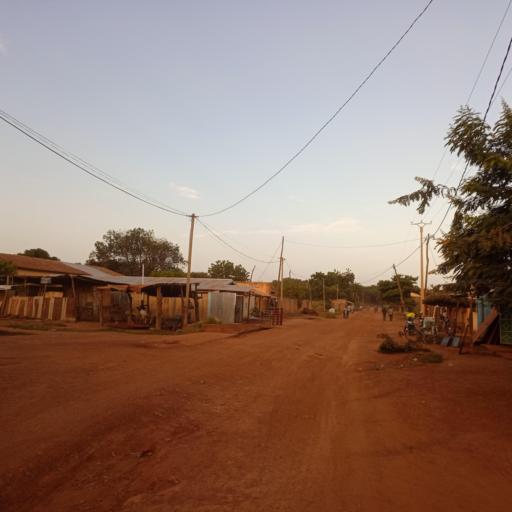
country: TG
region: Savanes
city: Dapaong
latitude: 10.8622
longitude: 0.1875
